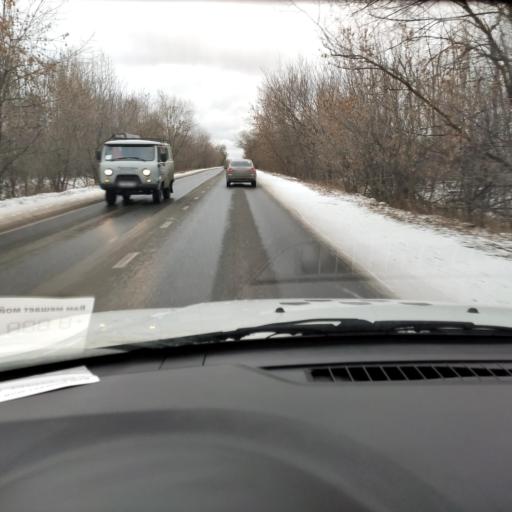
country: RU
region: Samara
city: Tol'yatti
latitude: 53.5478
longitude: 49.3936
